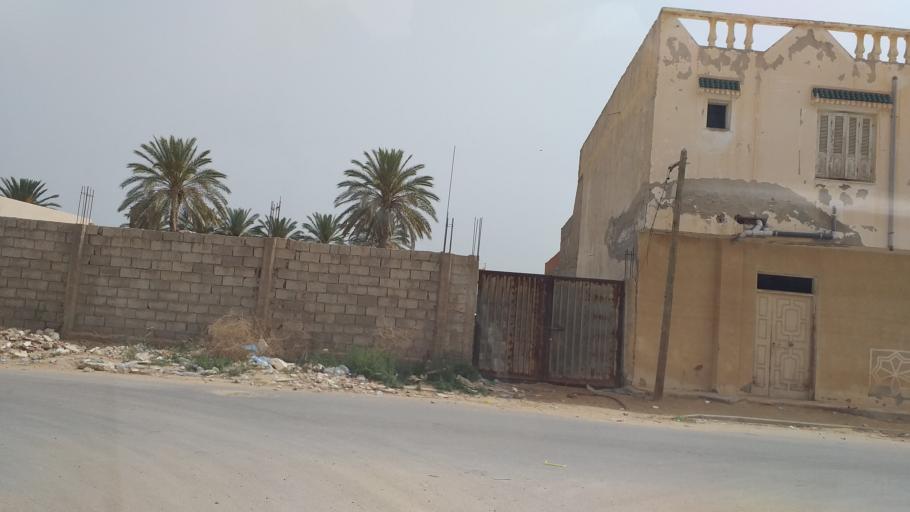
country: TN
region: Qabis
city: Gabes
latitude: 33.9434
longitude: 10.0568
